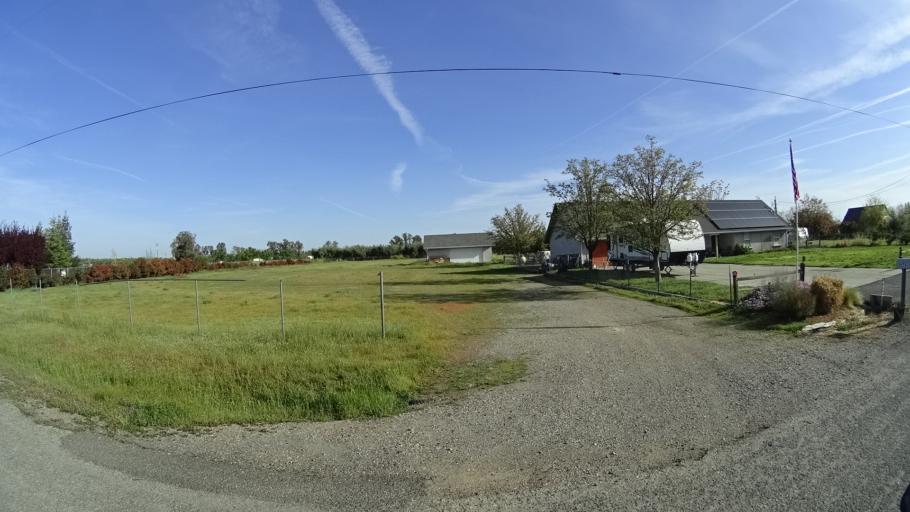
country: US
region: California
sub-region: Glenn County
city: Orland
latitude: 39.7222
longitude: -122.2091
